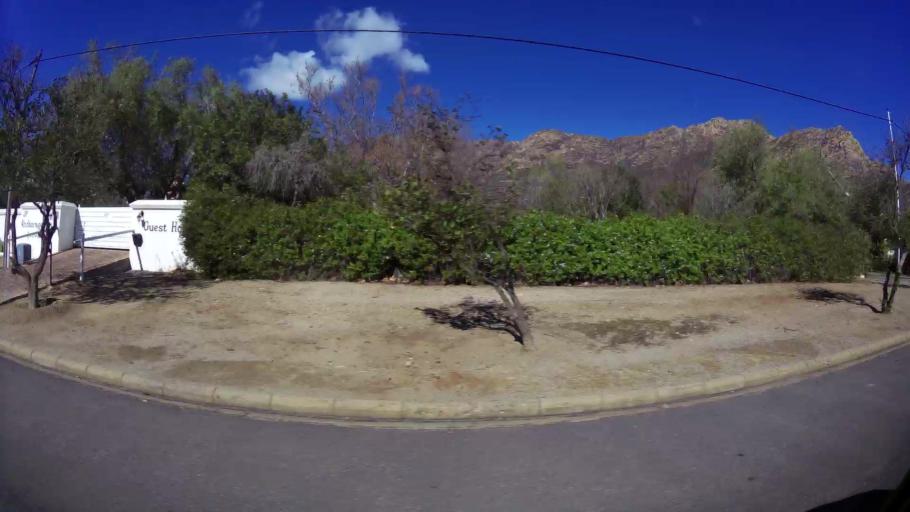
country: ZA
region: Western Cape
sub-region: Cape Winelands District Municipality
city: Ashton
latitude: -33.7938
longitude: 20.1189
